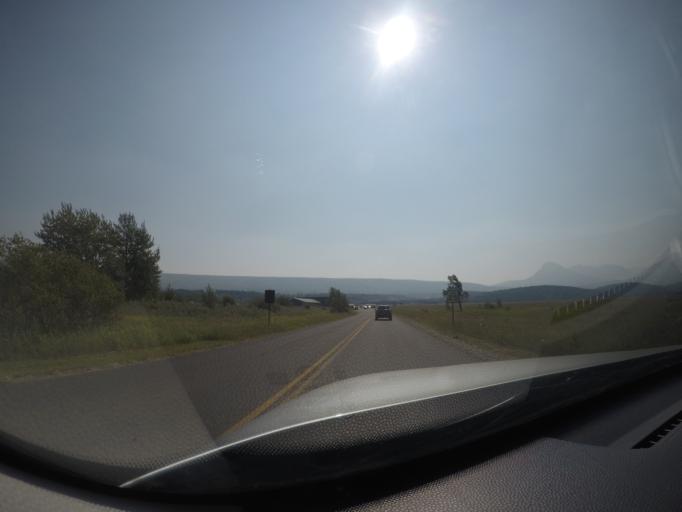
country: US
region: Montana
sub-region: Glacier County
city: North Browning
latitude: 48.7485
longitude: -113.4422
